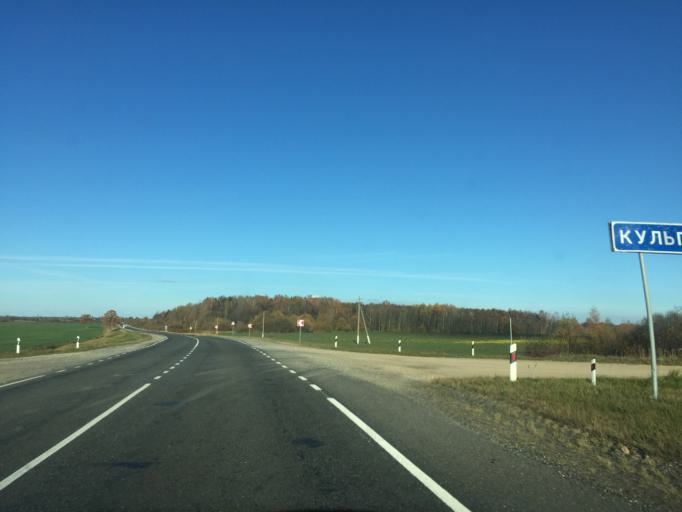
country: BY
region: Vitebsk
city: Dzisna
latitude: 55.3156
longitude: 28.2715
